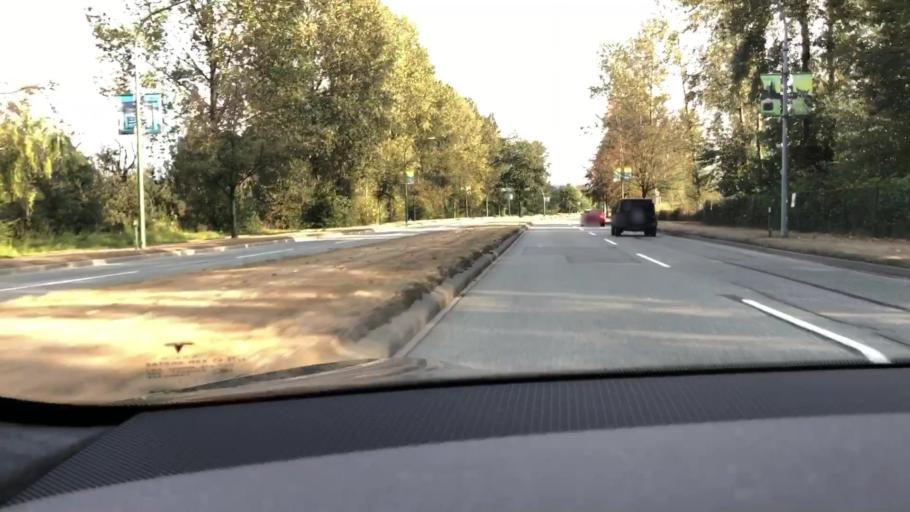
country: CA
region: British Columbia
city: Burnaby
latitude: 49.2570
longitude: -122.9678
